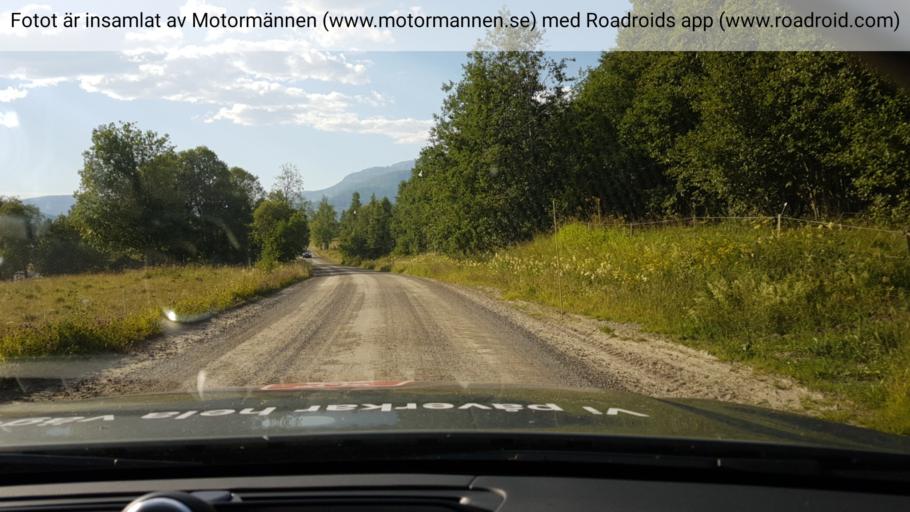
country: SE
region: Jaemtland
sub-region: Are Kommun
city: Are
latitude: 63.3621
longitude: 13.1699
